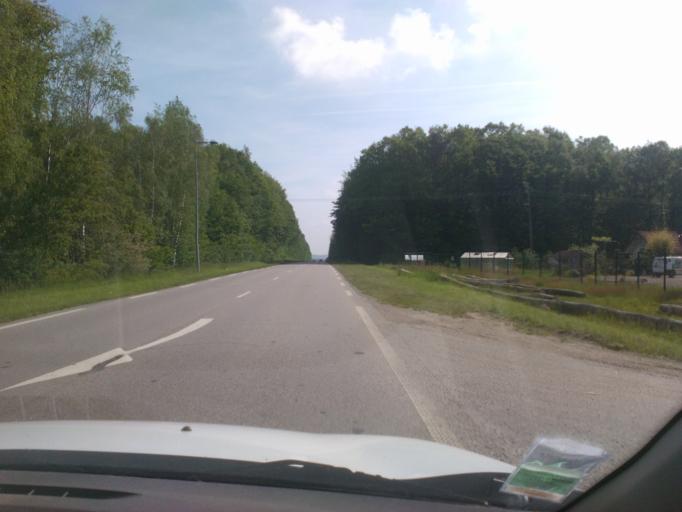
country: FR
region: Lorraine
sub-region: Departement des Vosges
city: Les Forges
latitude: 48.1934
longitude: 6.4040
